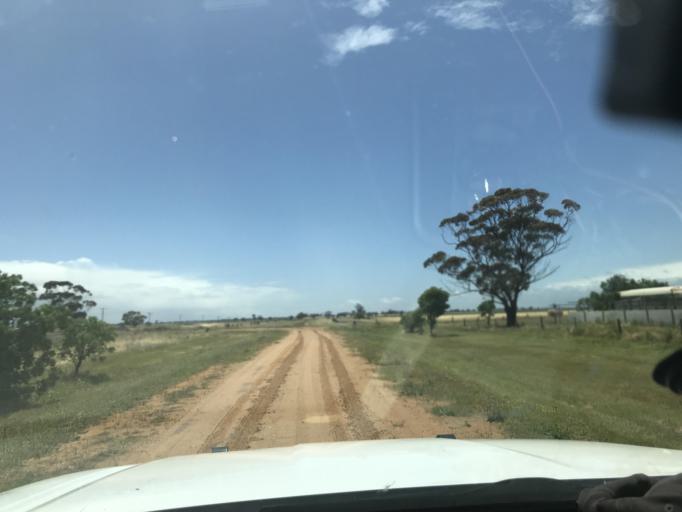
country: AU
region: South Australia
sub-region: Tatiara
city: Bordertown
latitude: -36.3758
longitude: 140.9904
